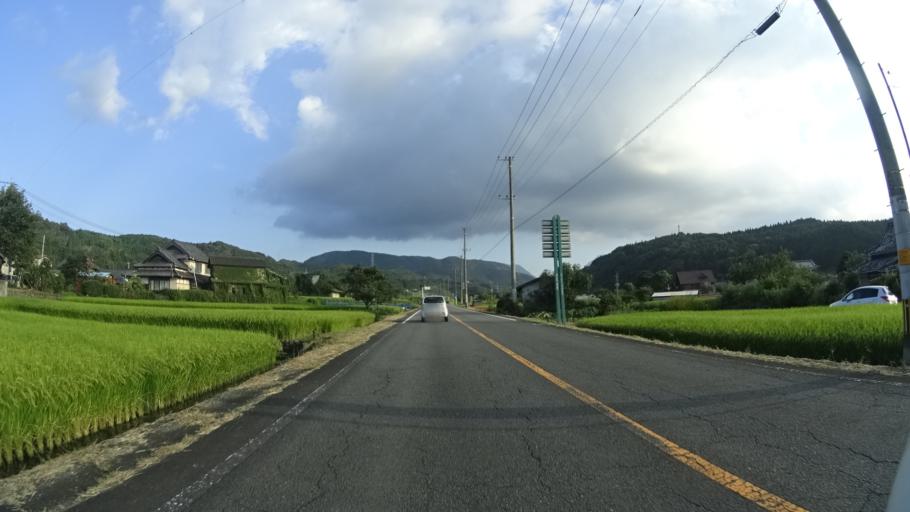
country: JP
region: Oita
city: Hiji
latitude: 33.3908
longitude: 131.3940
